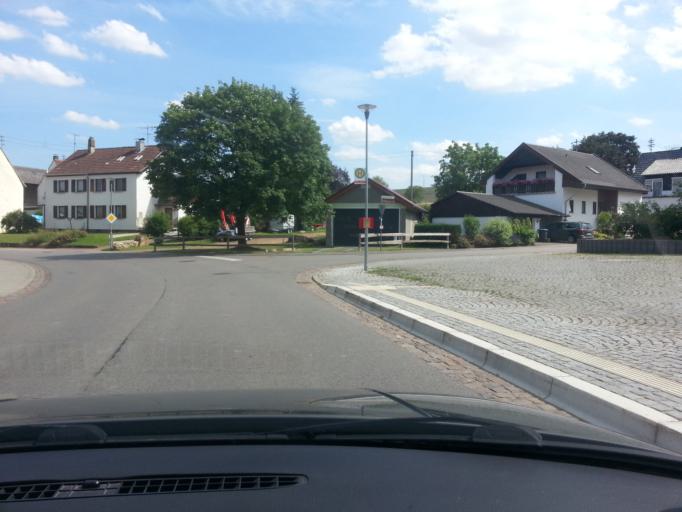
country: DE
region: Saarland
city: Blieskastel
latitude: 49.1821
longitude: 7.2922
